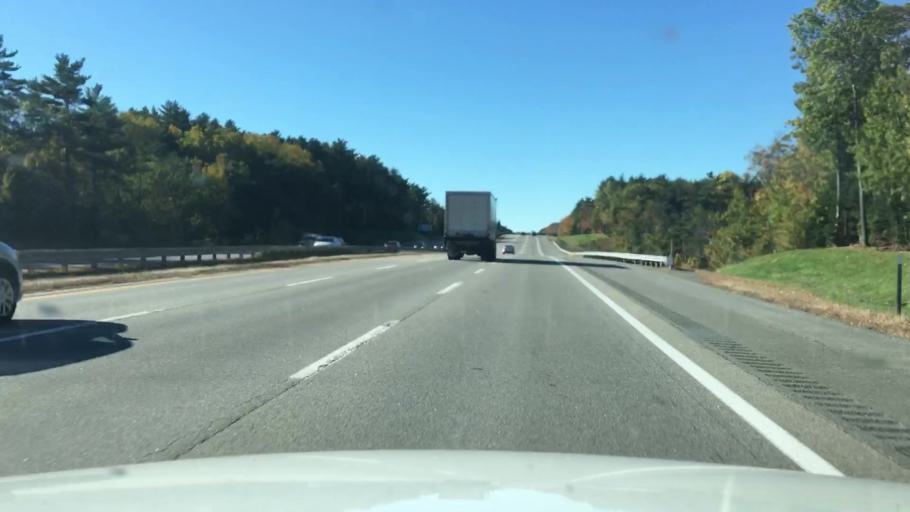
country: US
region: Maine
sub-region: Cumberland County
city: West Scarborough
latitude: 43.5819
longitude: -70.3956
